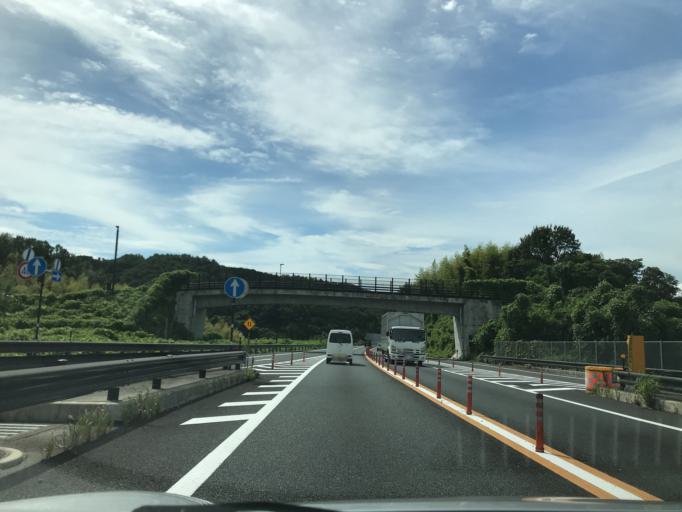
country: JP
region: Shizuoka
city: Mishima
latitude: 35.1198
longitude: 138.9496
